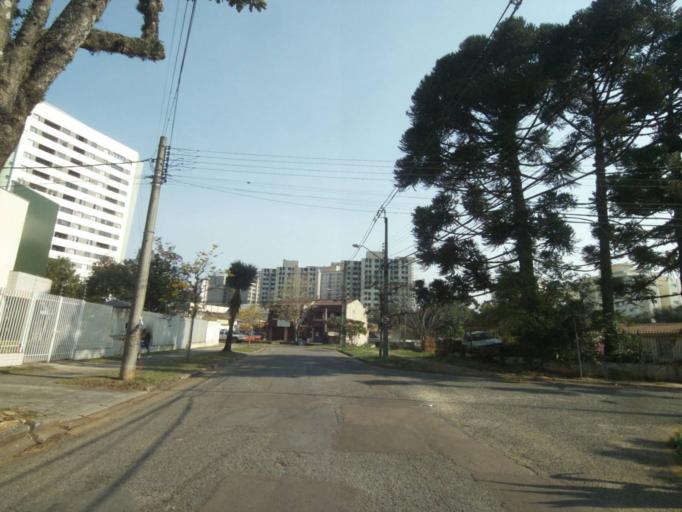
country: BR
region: Parana
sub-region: Curitiba
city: Curitiba
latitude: -25.4654
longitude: -49.2936
